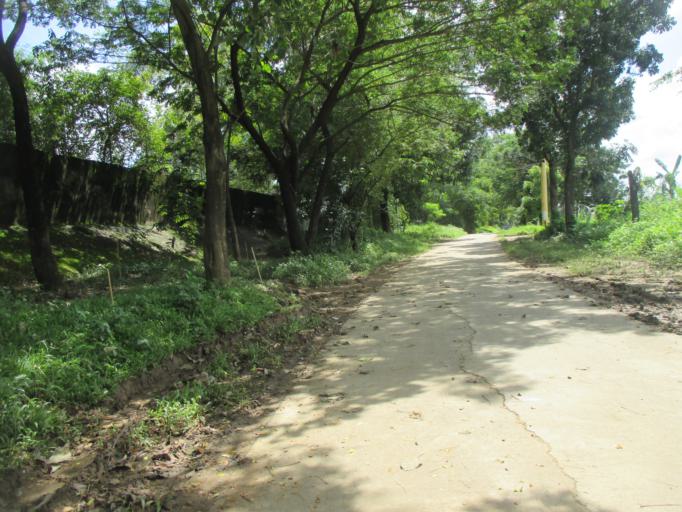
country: PH
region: Metro Manila
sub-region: Marikina
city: Calumpang
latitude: 14.6271
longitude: 121.0885
